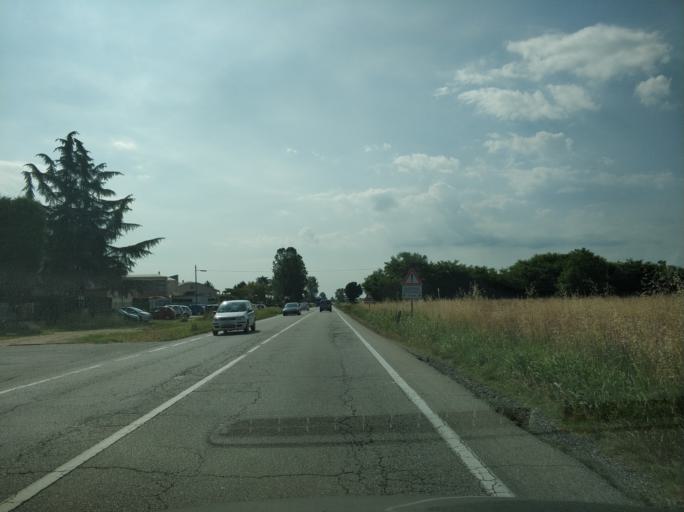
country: IT
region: Piedmont
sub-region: Provincia di Torino
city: Marocchi
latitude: 44.9520
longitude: 7.7971
